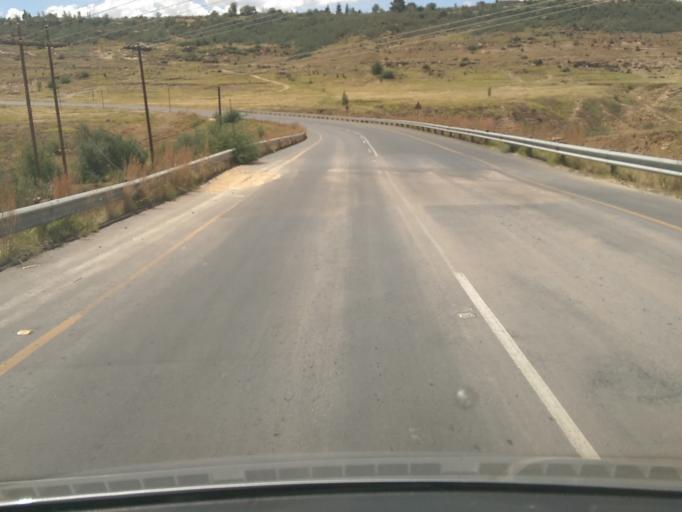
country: LS
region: Maseru
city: Maseru
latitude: -29.3831
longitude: 27.5035
